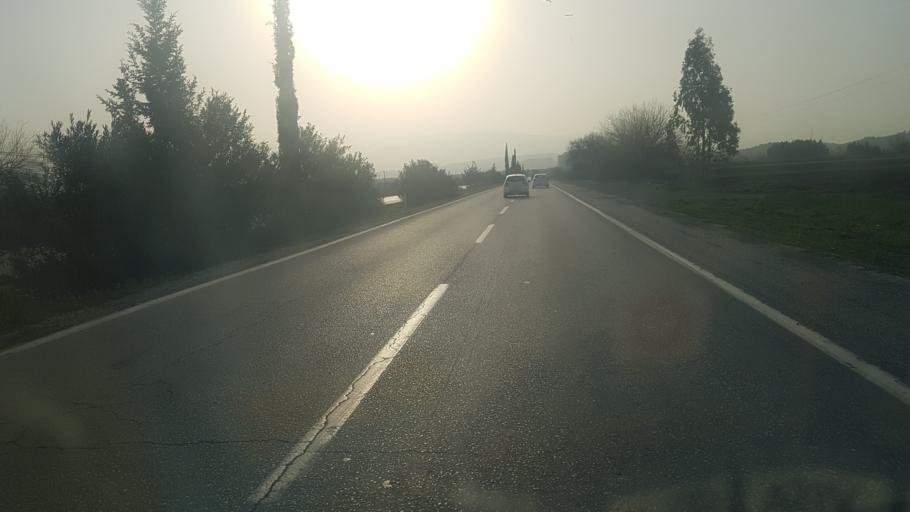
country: TR
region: Osmaniye
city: Toprakkale
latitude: 37.0684
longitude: 36.0970
